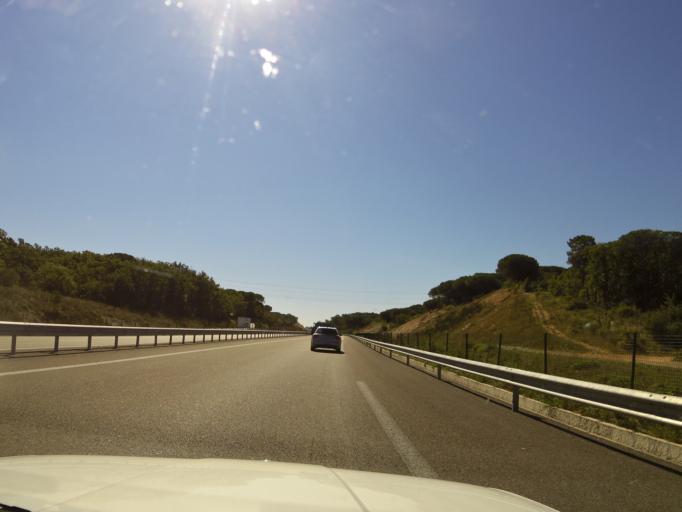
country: FR
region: Languedoc-Roussillon
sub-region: Departement du Gard
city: La Calmette
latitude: 43.9165
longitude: 4.2625
